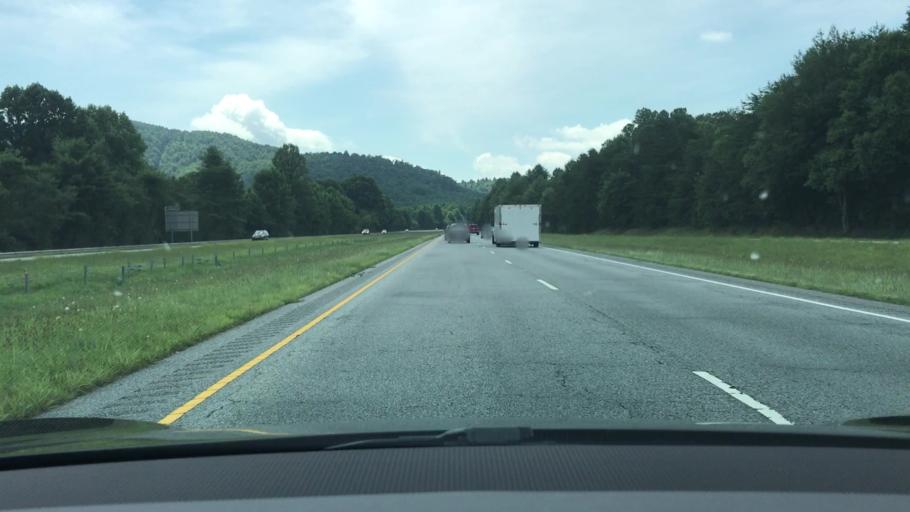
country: US
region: North Carolina
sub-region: Henderson County
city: Flat Rock
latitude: 35.1854
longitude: -82.4482
